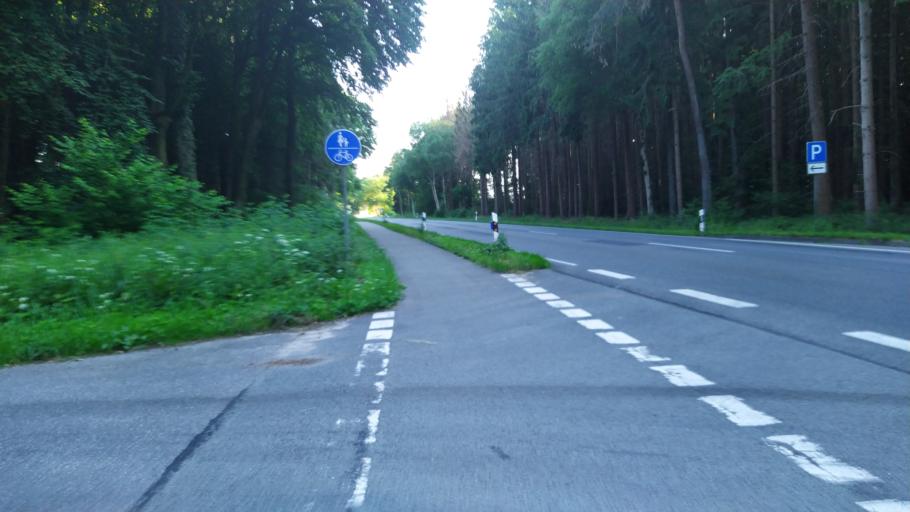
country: DE
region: Lower Saxony
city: Alfstedt
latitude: 53.5375
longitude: 9.0554
